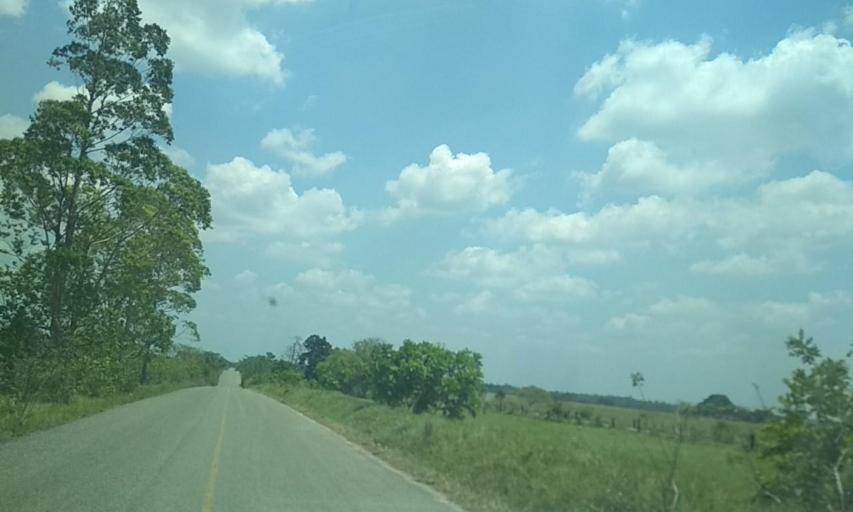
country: MX
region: Tabasco
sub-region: Huimanguillo
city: Francisco Rueda
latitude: 17.8039
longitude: -93.8614
